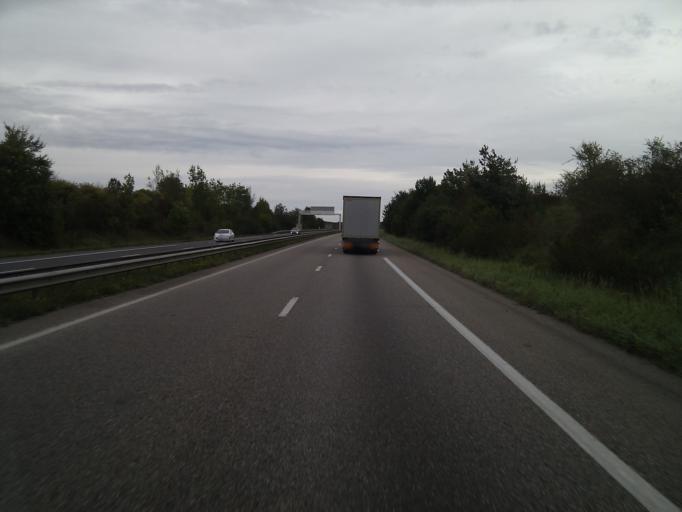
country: FR
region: Lorraine
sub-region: Departement de Meurthe-et-Moselle
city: Gondreville
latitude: 48.6885
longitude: 5.9690
